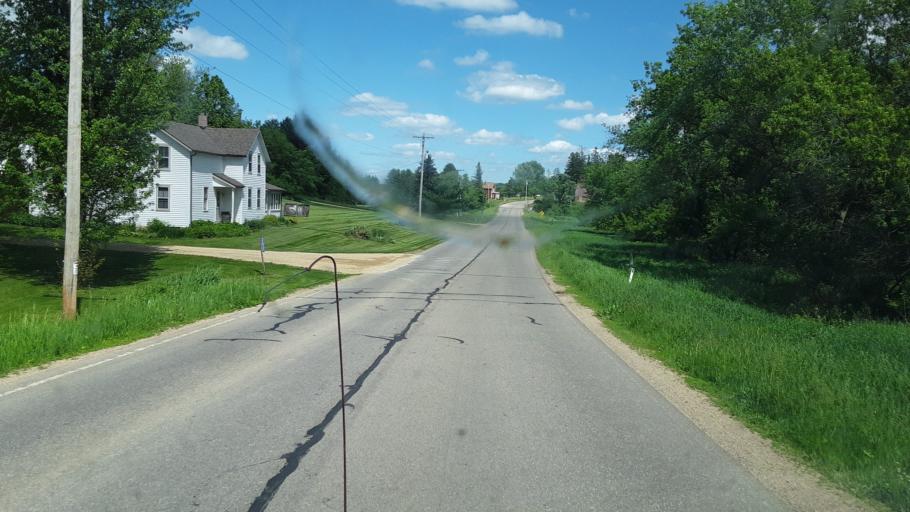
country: US
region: Wisconsin
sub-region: Vernon County
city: Hillsboro
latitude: 43.5261
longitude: -90.2135
